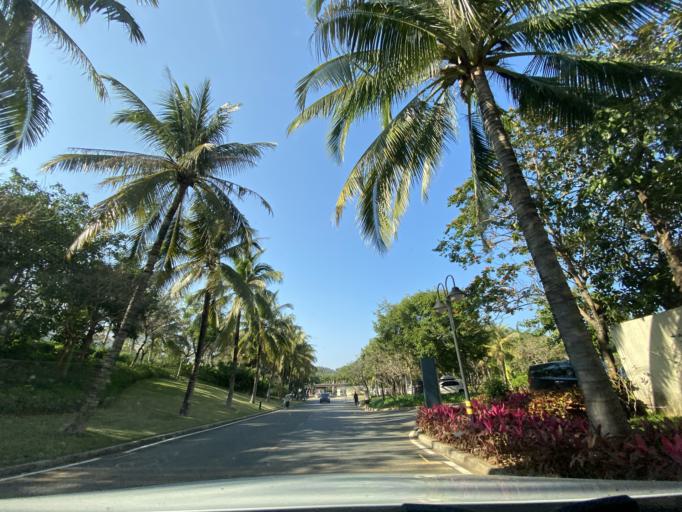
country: CN
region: Hainan
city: Yingzhou
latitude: 18.4182
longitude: 109.8962
